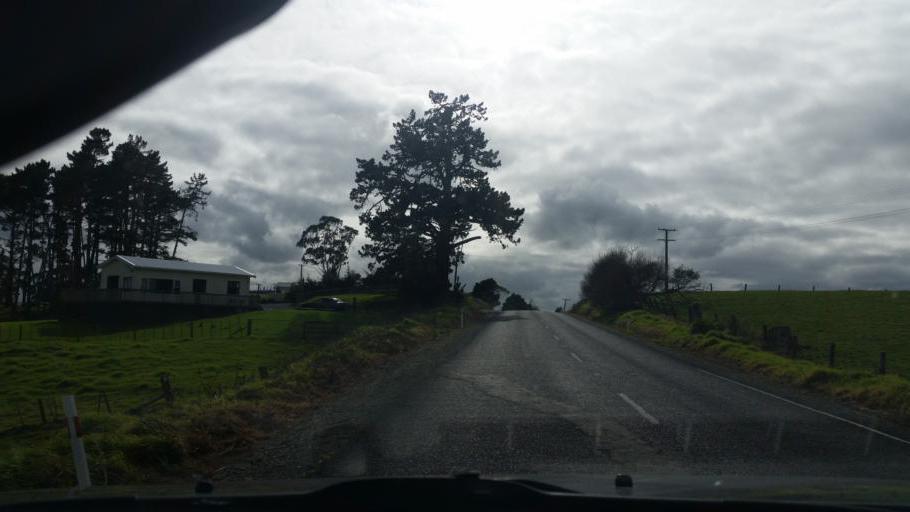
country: NZ
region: Northland
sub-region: Whangarei
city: Ruakaka
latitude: -36.1278
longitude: 174.2300
